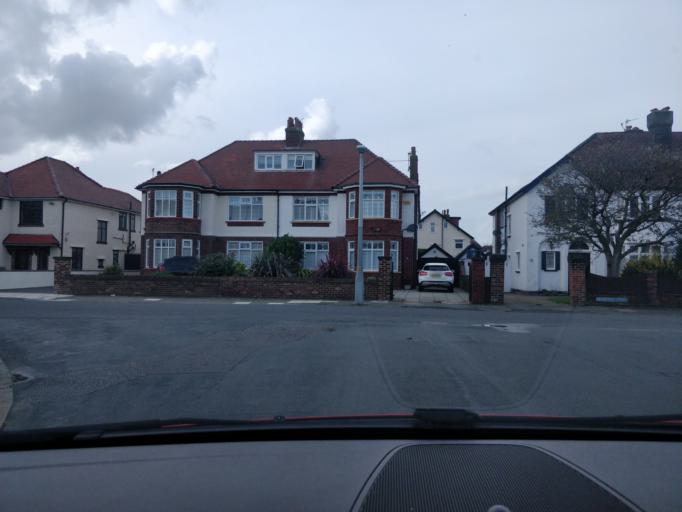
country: GB
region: England
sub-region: Sefton
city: Southport
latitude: 53.6236
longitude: -3.0202
